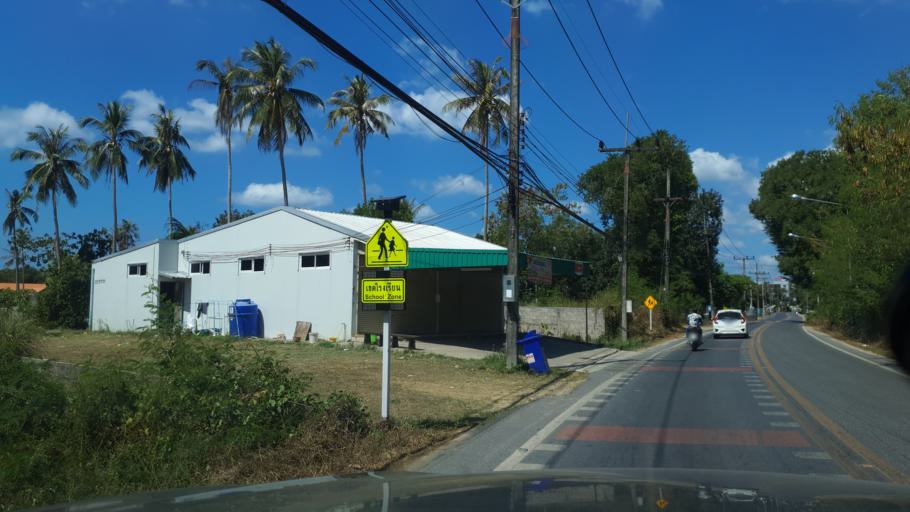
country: TH
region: Phuket
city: Thalang
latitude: 8.1305
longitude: 98.3078
